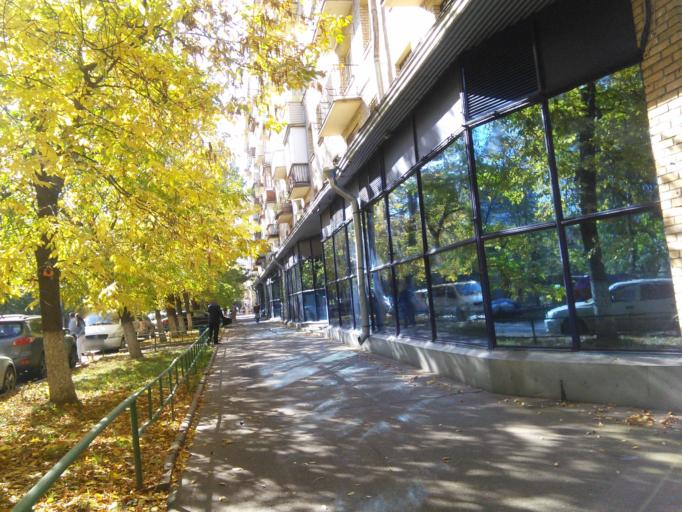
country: RU
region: Moskovskaya
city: Leninskiye Gory
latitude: 55.6948
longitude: 37.5737
